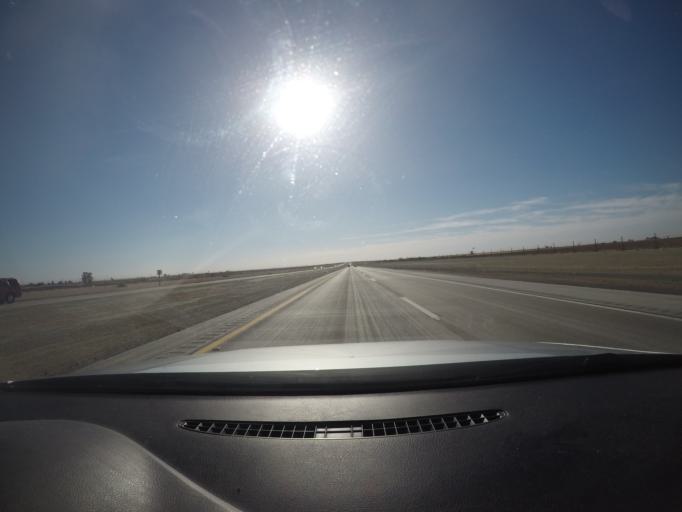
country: US
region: California
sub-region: Imperial County
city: Holtville
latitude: 32.7732
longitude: -115.3559
